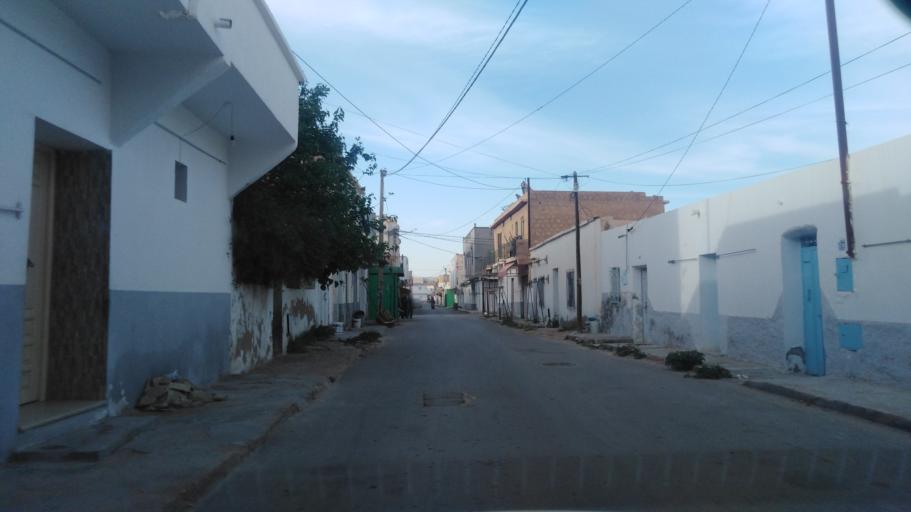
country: TN
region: Tataouine
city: Tataouine
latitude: 32.9352
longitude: 10.4527
